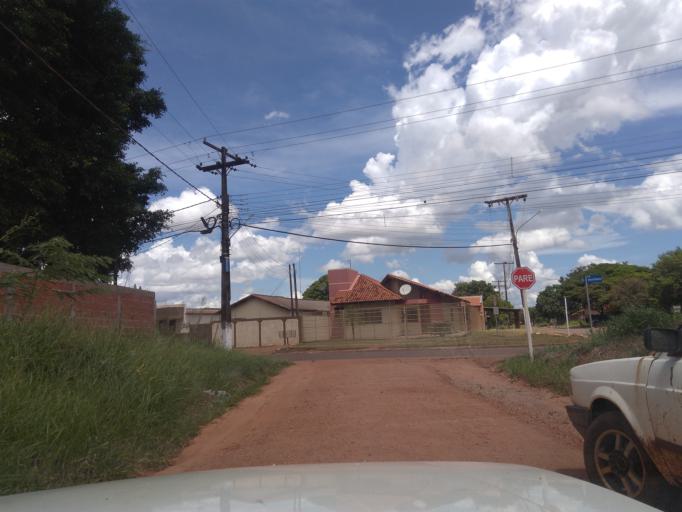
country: BR
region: Mato Grosso do Sul
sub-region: Ponta Pora
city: Ponta Pora
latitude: -22.5045
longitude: -55.7307
